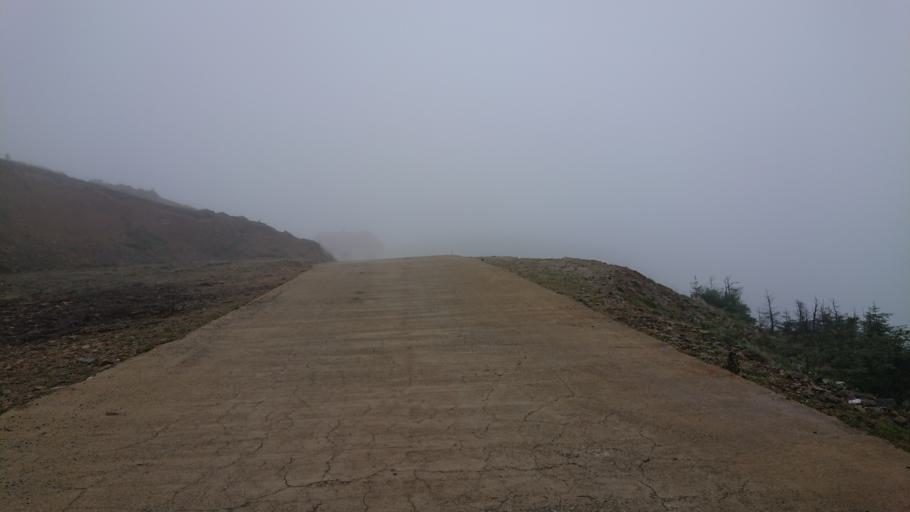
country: TR
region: Gumushane
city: Kurtun
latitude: 40.6719
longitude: 38.9985
